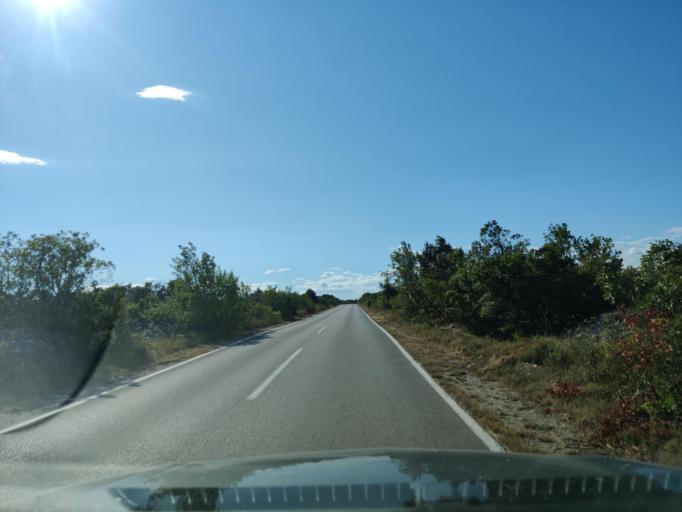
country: HR
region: Sibensko-Kniniska
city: Zaton
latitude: 43.7438
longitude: 15.8502
